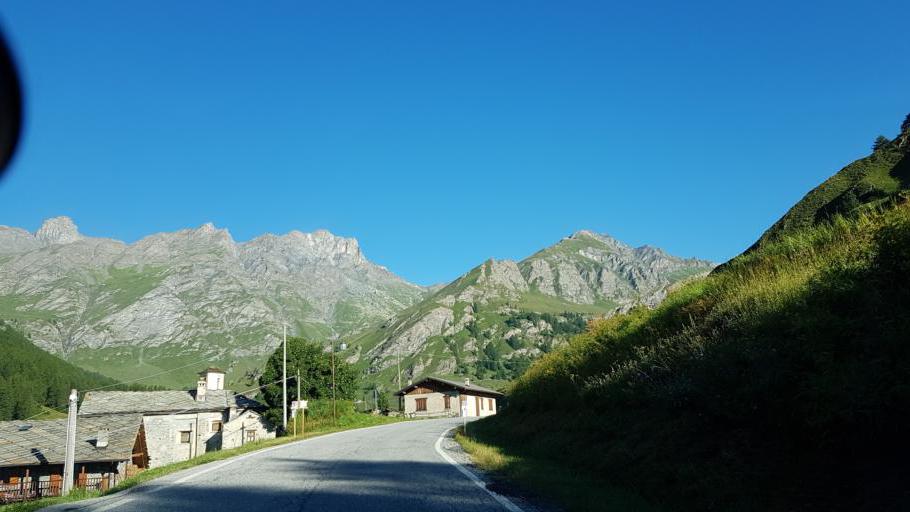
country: IT
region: Piedmont
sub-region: Provincia di Cuneo
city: Pontechianale
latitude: 44.6461
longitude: 7.0010
